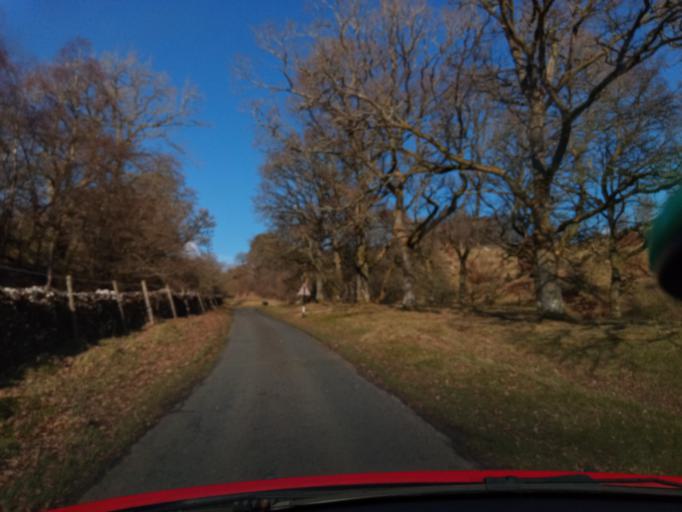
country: GB
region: Scotland
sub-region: The Scottish Borders
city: Hawick
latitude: 55.4205
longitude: -2.8700
